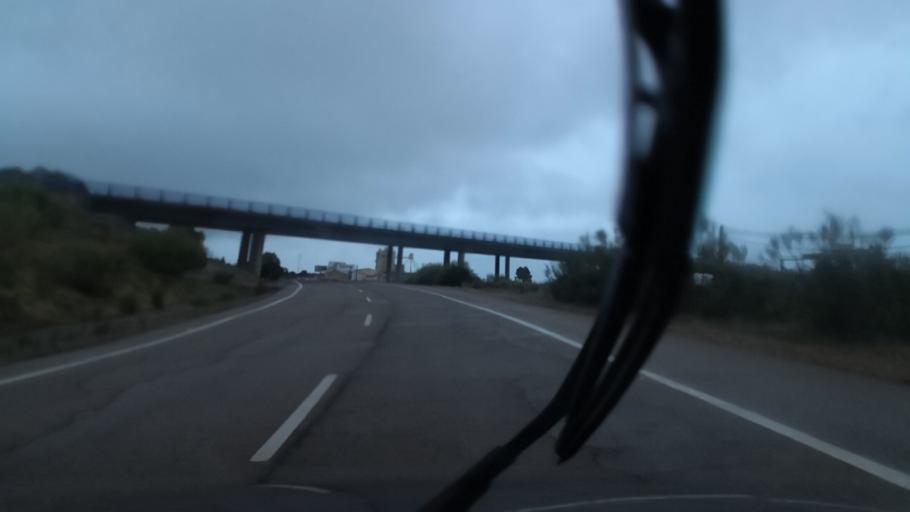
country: ES
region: Extremadura
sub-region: Provincia de Badajoz
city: Calamonte
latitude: 38.9048
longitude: -6.3741
